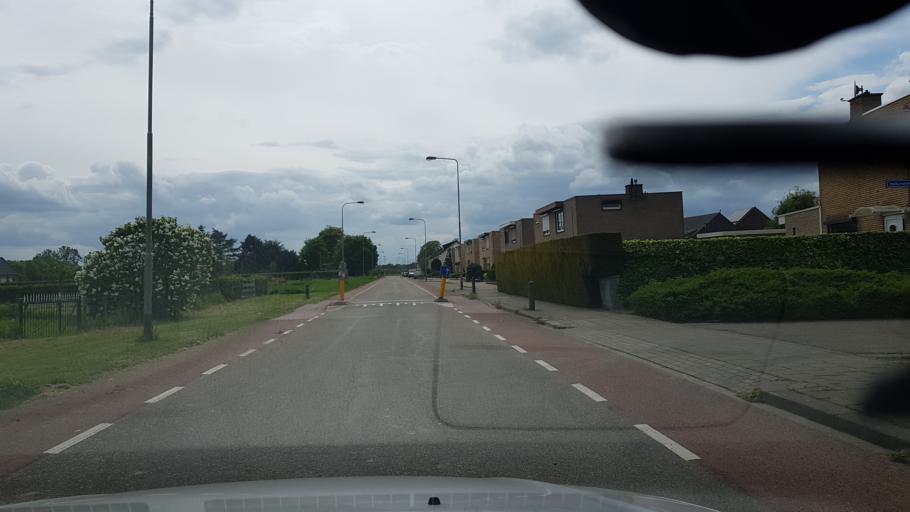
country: NL
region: Limburg
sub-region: Gemeente Sittard-Geleen
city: Born
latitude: 51.0470
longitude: 5.8253
